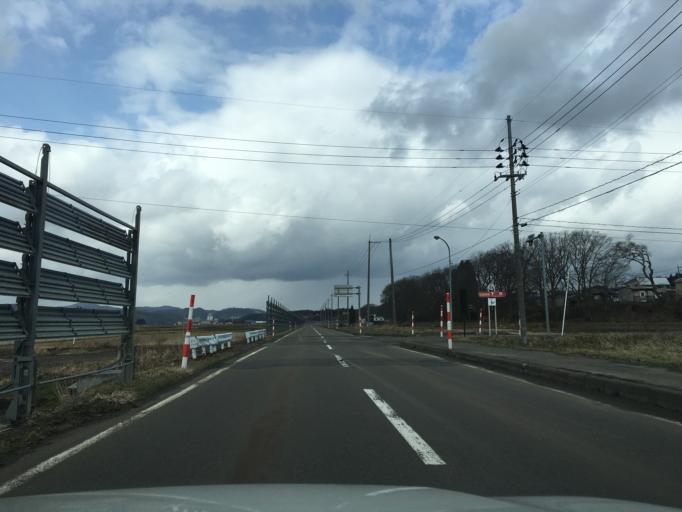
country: JP
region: Akita
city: Takanosu
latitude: 40.1492
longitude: 140.3400
